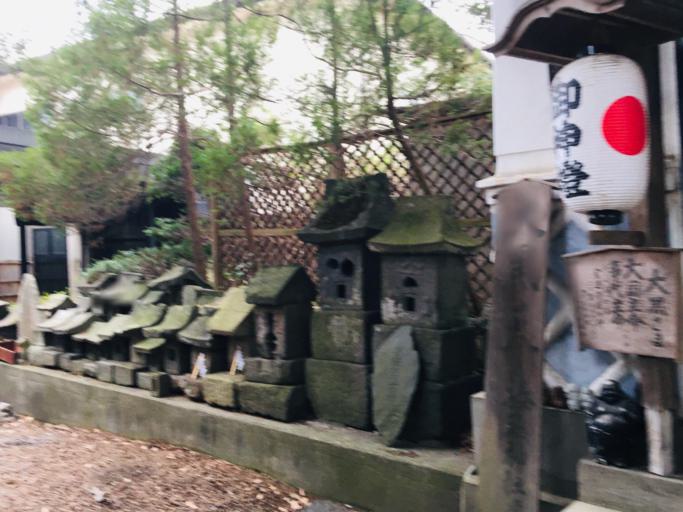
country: JP
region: Gunma
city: Numata
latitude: 36.6488
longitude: 139.0353
